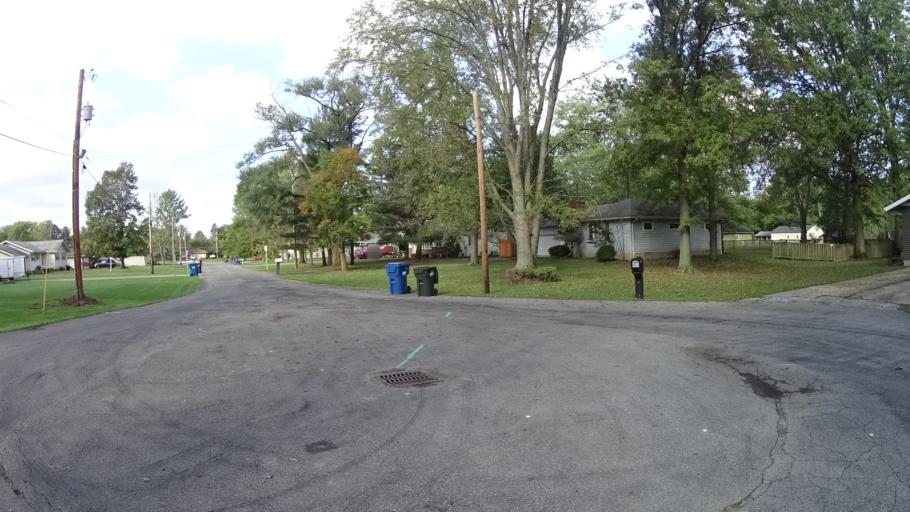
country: US
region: Ohio
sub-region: Lorain County
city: Grafton
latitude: 41.3139
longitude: -82.0785
